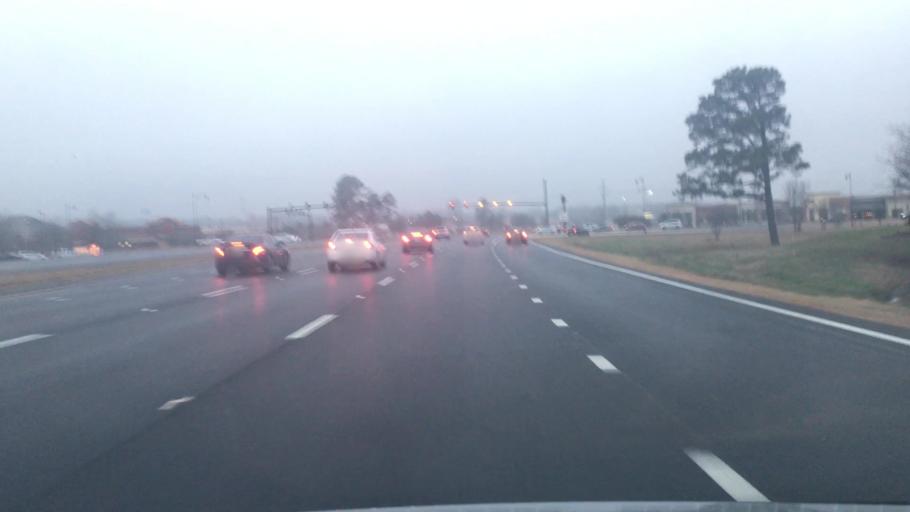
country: US
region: Mississippi
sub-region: Rankin County
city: Flowood
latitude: 32.3405
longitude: -90.0624
